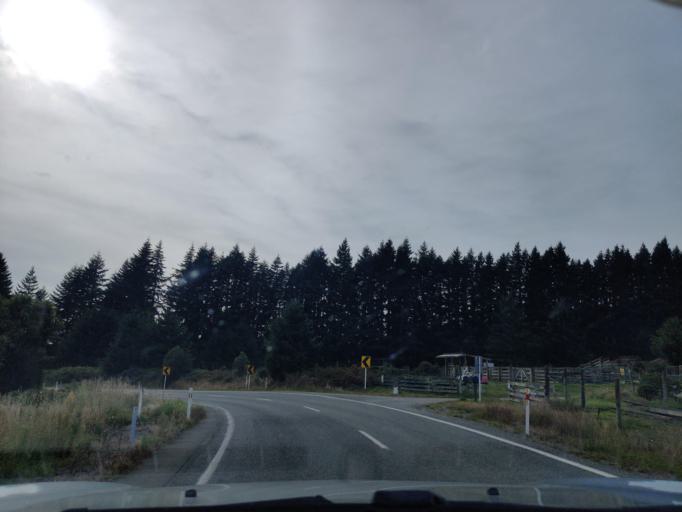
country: NZ
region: Tasman
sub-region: Tasman District
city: Brightwater
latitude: -41.6853
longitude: 173.1623
